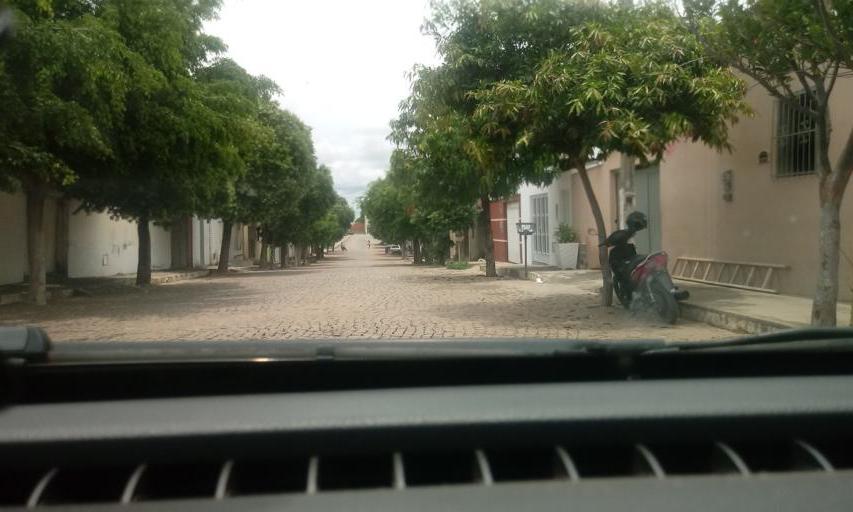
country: BR
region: Bahia
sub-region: Riacho De Santana
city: Riacho de Santana
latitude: -13.9092
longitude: -42.8448
